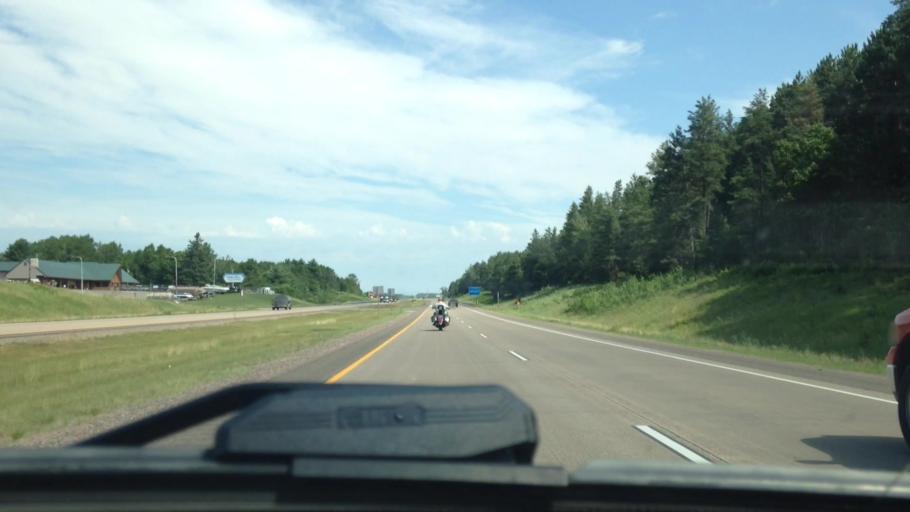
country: US
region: Wisconsin
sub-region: Washburn County
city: Spooner
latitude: 45.8891
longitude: -91.8277
